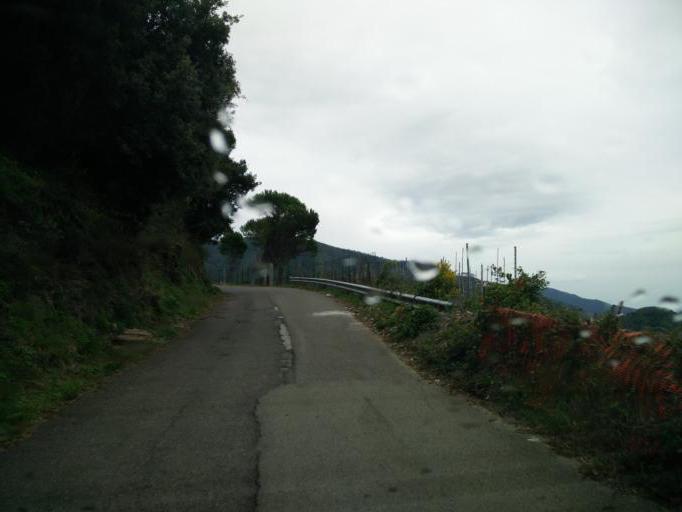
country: IT
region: Liguria
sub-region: Provincia di La Spezia
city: Vernazza
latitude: 44.1429
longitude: 9.6840
